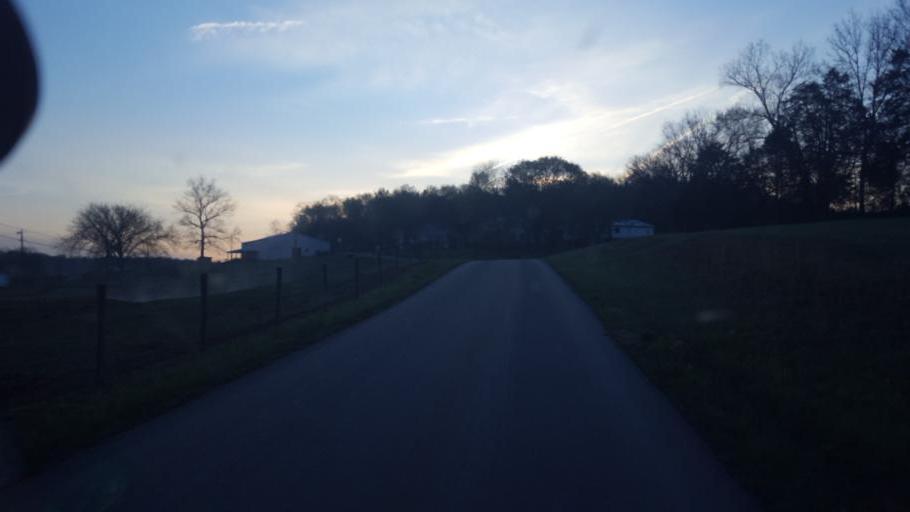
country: US
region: Kentucky
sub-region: Hart County
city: Munfordville
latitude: 37.2660
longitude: -85.9614
